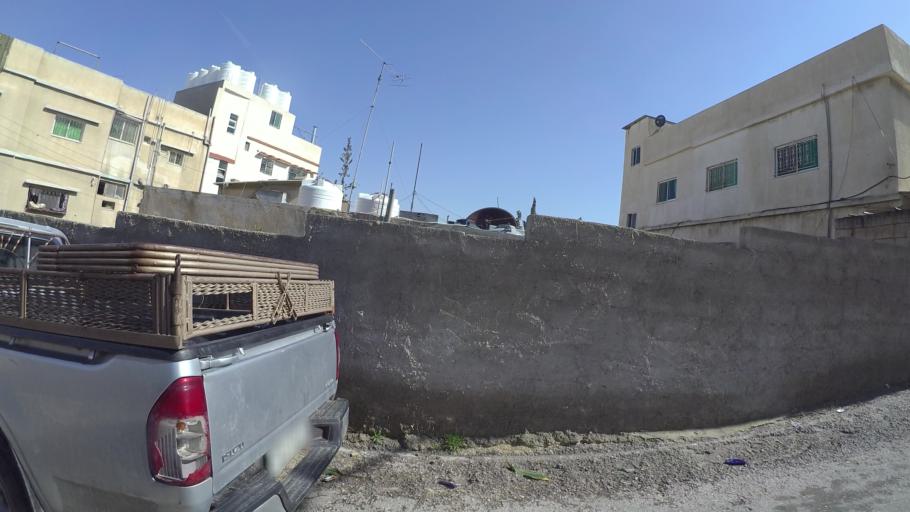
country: JO
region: Amman
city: Amman
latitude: 31.9881
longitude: 35.9860
